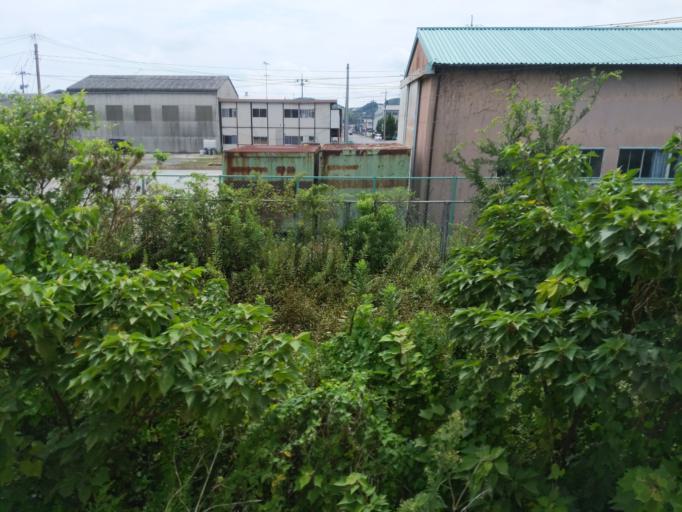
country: JP
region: Okayama
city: Okayama-shi
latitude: 34.6851
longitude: 133.9810
